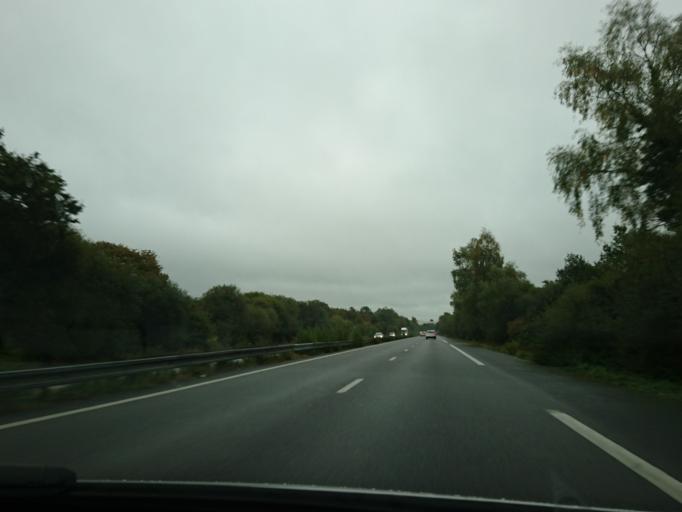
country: FR
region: Brittany
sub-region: Departement du Morbihan
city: Nostang
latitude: 47.7663
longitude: -3.1568
